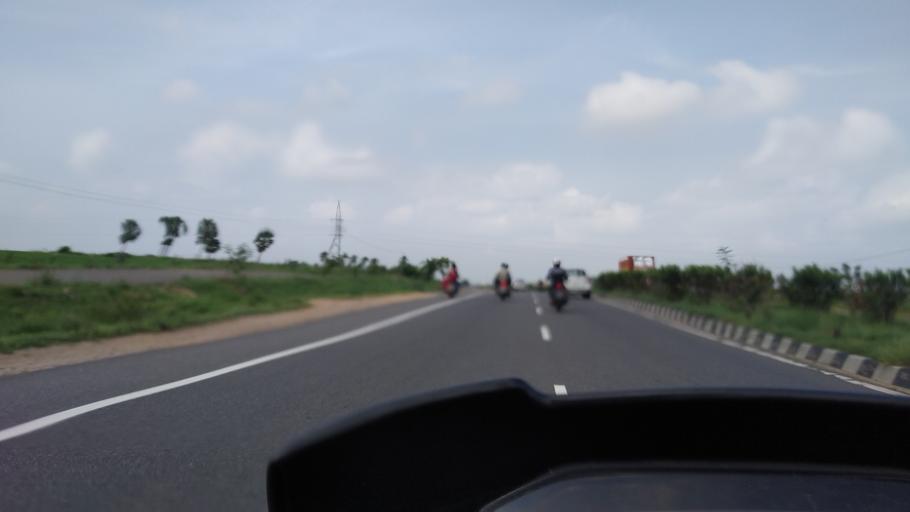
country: IN
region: Tamil Nadu
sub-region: Erode
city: Bhavani
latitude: 11.4480
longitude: 77.7563
